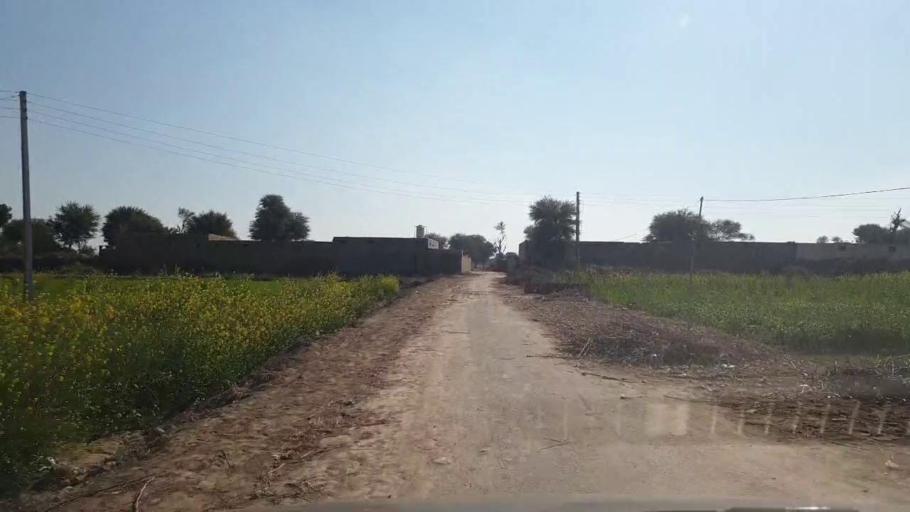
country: PK
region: Sindh
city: Shahpur Chakar
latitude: 26.1063
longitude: 68.6630
